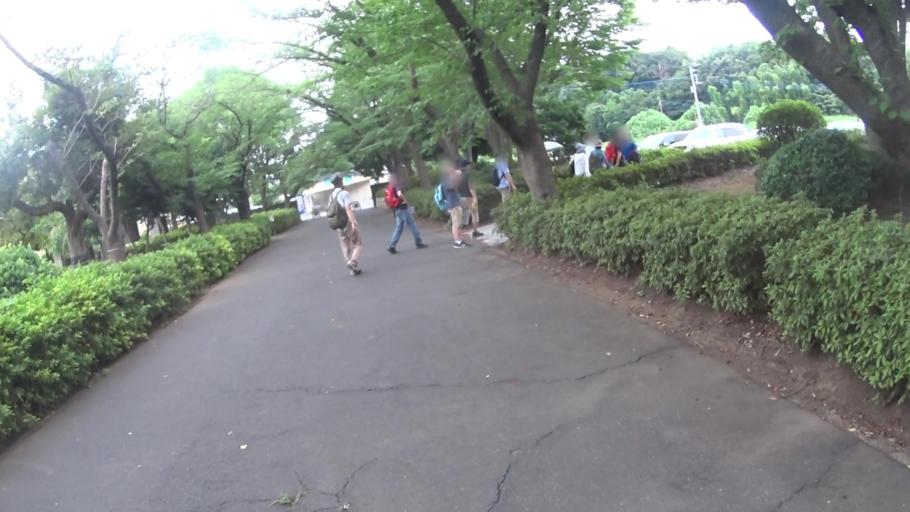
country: JP
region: Saitama
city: Okegawa
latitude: 35.9540
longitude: 139.5492
